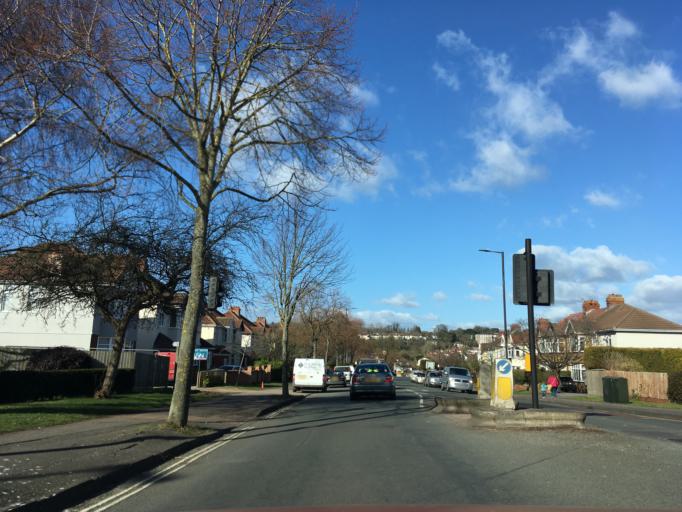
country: GB
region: England
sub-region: Bristol
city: Bristol
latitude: 51.4908
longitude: -2.6214
